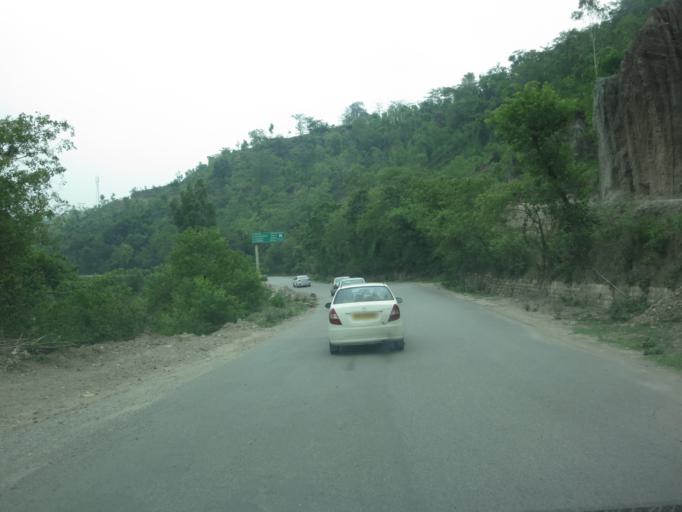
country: IN
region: Himachal Pradesh
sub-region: Mandi
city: Sundarnagar
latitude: 31.4440
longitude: 76.8552
